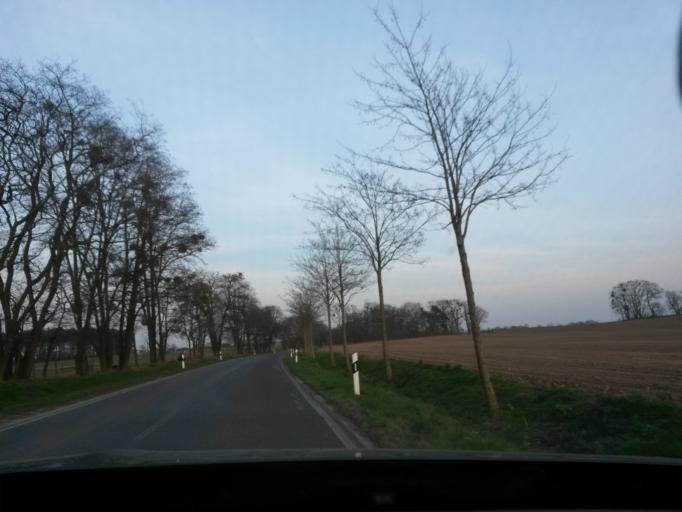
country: DE
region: Brandenburg
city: Strausberg
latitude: 52.5962
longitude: 13.9384
